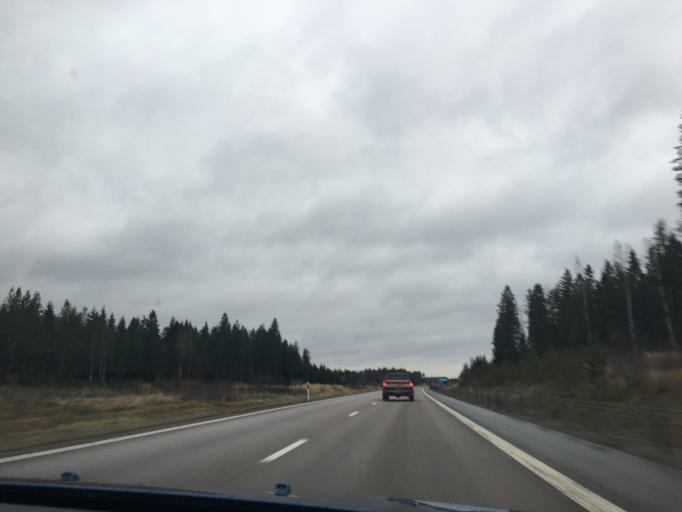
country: SE
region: Uppsala
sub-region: Tierps Kommun
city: Tierp
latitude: 60.4274
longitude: 17.4329
